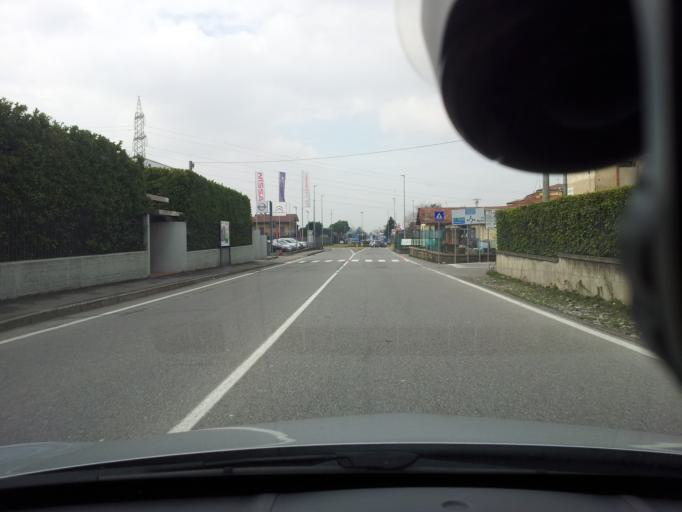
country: IT
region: Lombardy
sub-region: Provincia di Bergamo
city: Grumello del Monte
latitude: 45.6385
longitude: 9.8910
